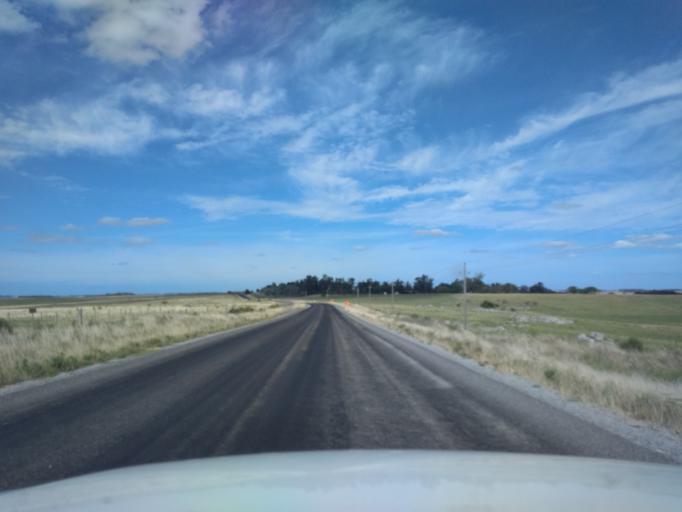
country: UY
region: Florida
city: Casupa
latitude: -34.0263
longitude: -55.8659
